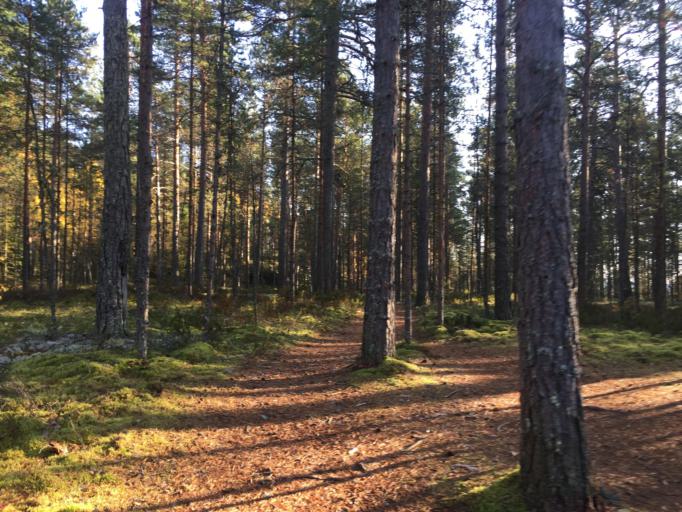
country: RU
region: Leningrad
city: Priozersk
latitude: 61.2816
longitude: 30.1123
